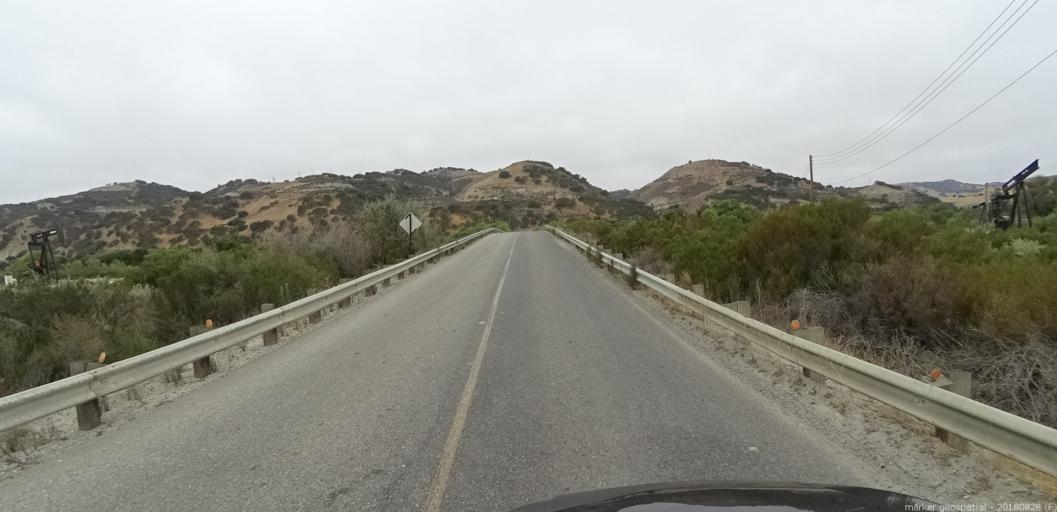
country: US
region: California
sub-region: San Luis Obispo County
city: Lake Nacimiento
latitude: 35.9629
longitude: -120.8783
